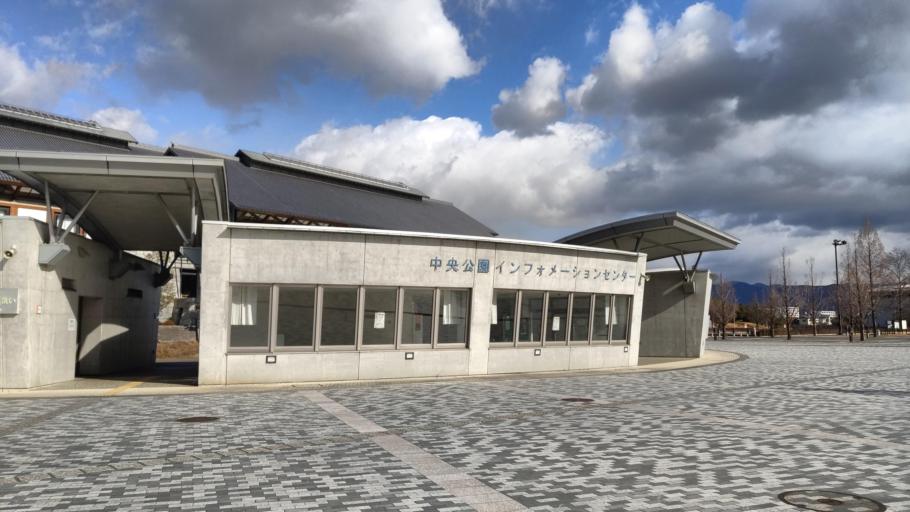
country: JP
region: Ehime
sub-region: Shikoku-chuo Shi
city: Matsuyama
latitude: 33.8093
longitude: 132.7452
